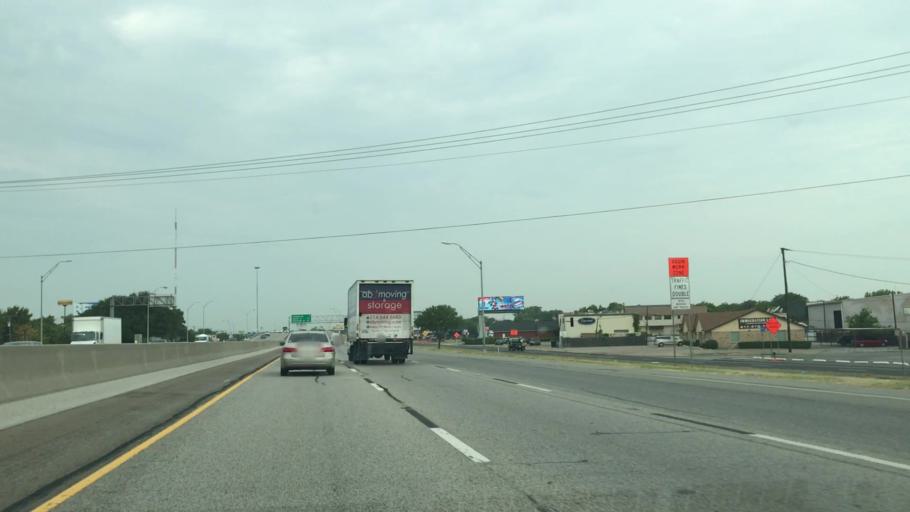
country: US
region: Texas
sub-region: Tarrant County
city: Haltom City
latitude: 32.7906
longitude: -97.2506
